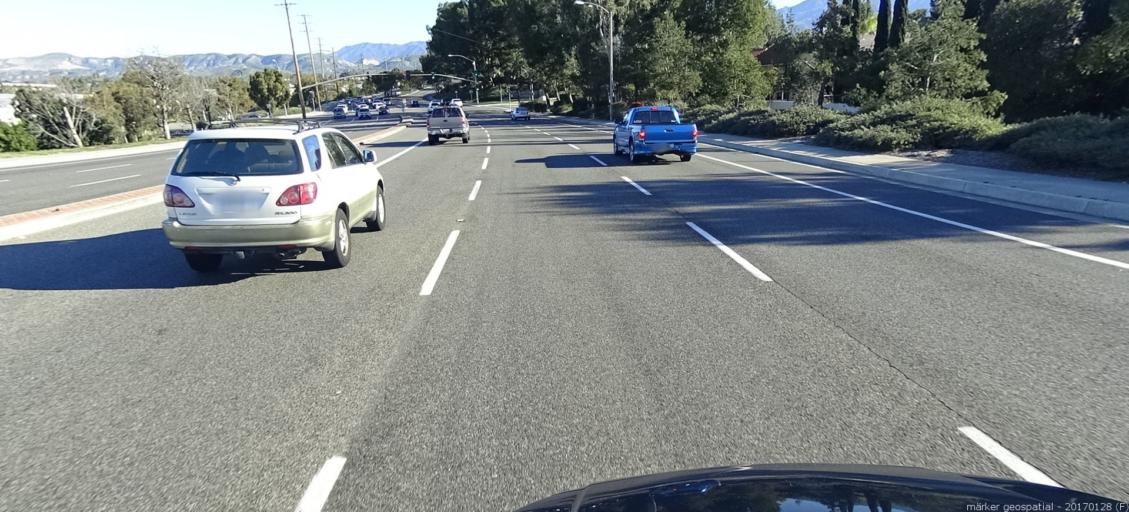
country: US
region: California
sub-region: Orange County
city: Lake Forest
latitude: 33.6438
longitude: -117.7119
